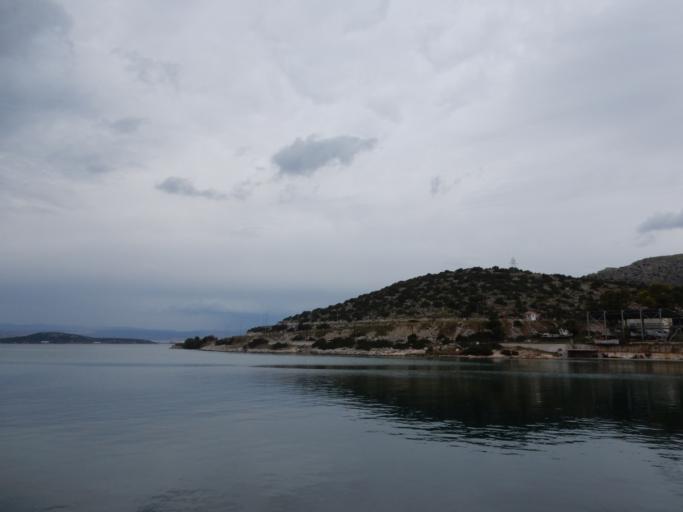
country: GR
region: Attica
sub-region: Nomos Piraios
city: Perama
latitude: 37.9648
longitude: 23.5549
